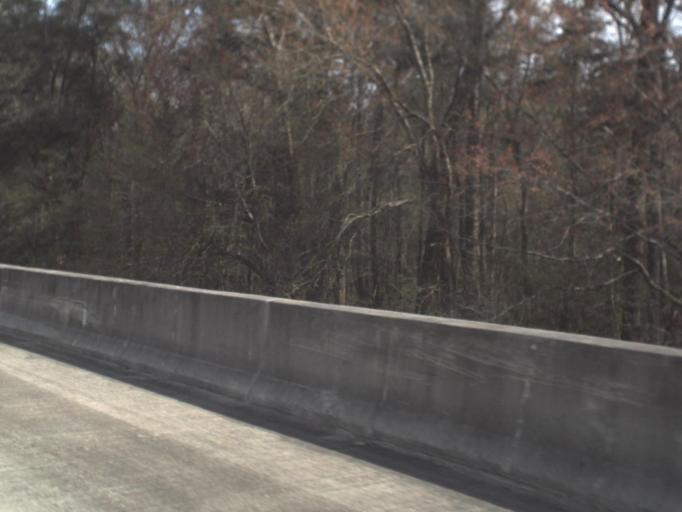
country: US
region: Florida
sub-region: Gadsden County
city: Midway
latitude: 30.4849
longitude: -84.3961
